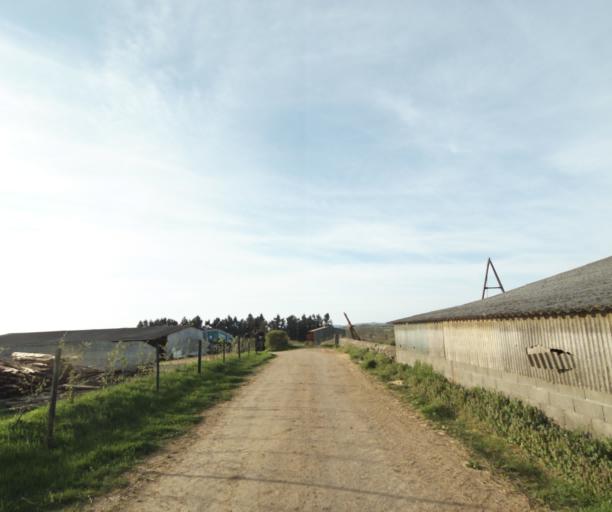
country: FR
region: Bourgogne
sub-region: Departement de Saone-et-Loire
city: Charolles
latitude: 46.4274
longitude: 4.3129
